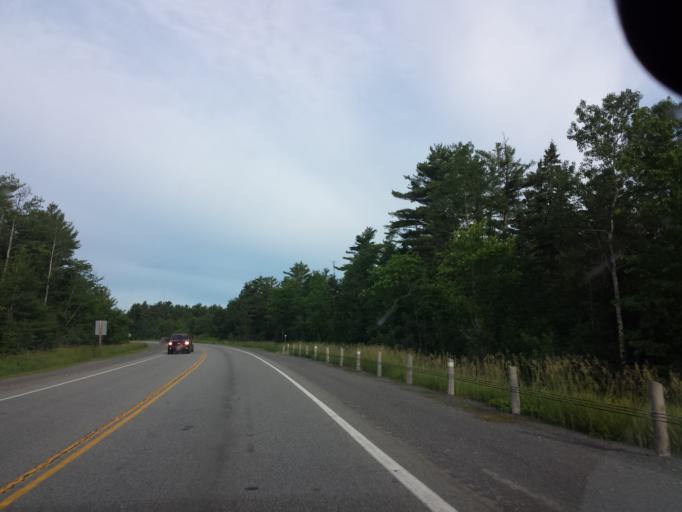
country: CA
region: Ontario
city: Arnprior
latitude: 45.4425
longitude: -76.4764
